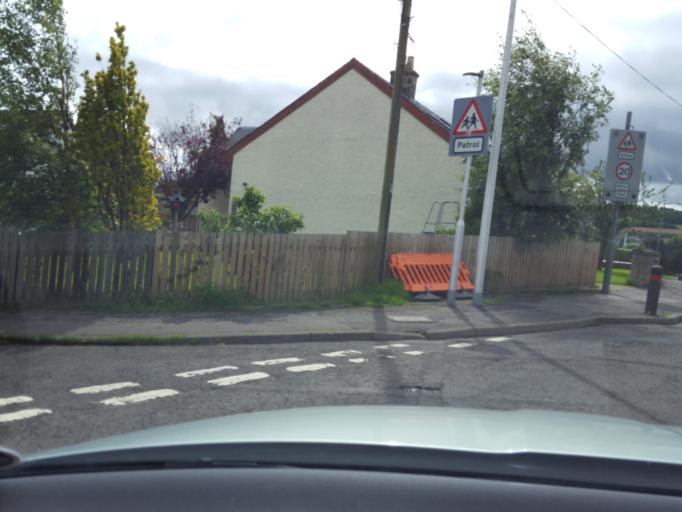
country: GB
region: Scotland
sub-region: Falkirk
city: Bo'ness
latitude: 56.0122
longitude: -3.5996
